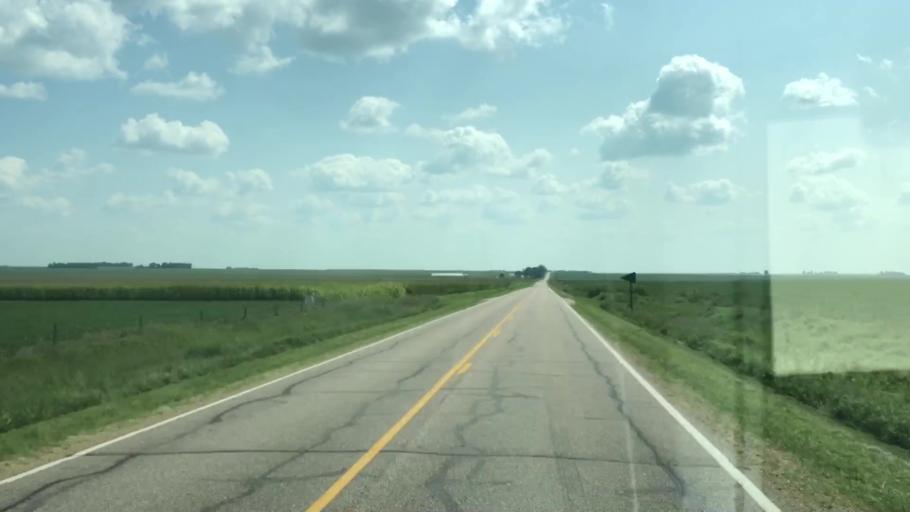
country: US
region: Iowa
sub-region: O'Brien County
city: Sheldon
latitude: 43.1649
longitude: -95.8019
